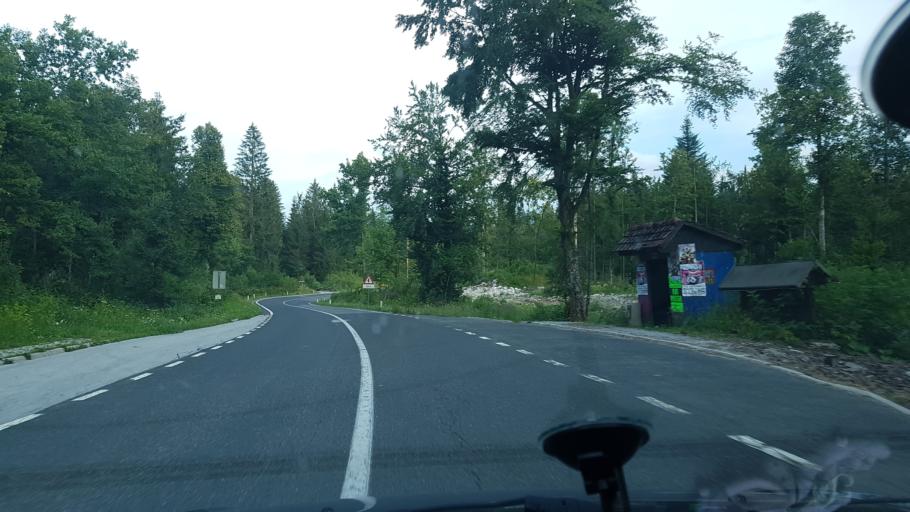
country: SI
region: Logatec
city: Logatec
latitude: 45.9093
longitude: 14.1610
